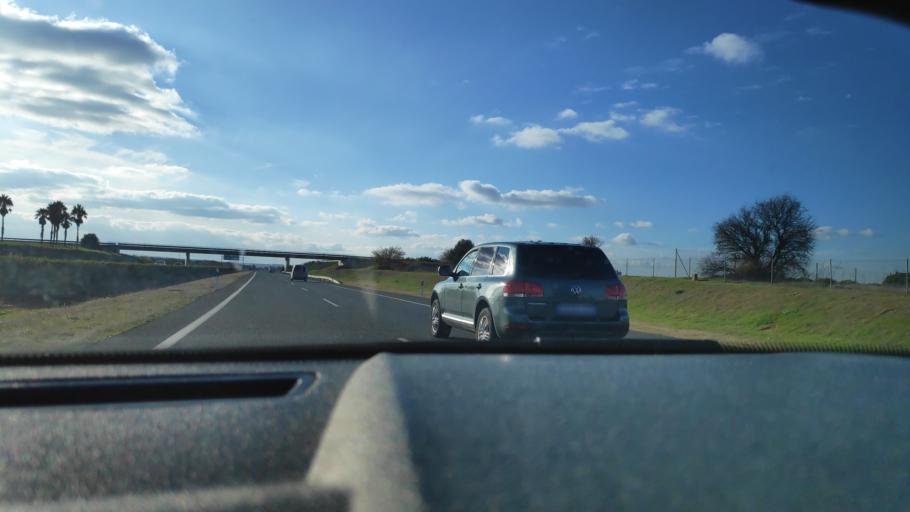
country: ES
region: Andalusia
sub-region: Provincia de Sevilla
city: La Luisiana
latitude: 37.5258
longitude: -5.2347
